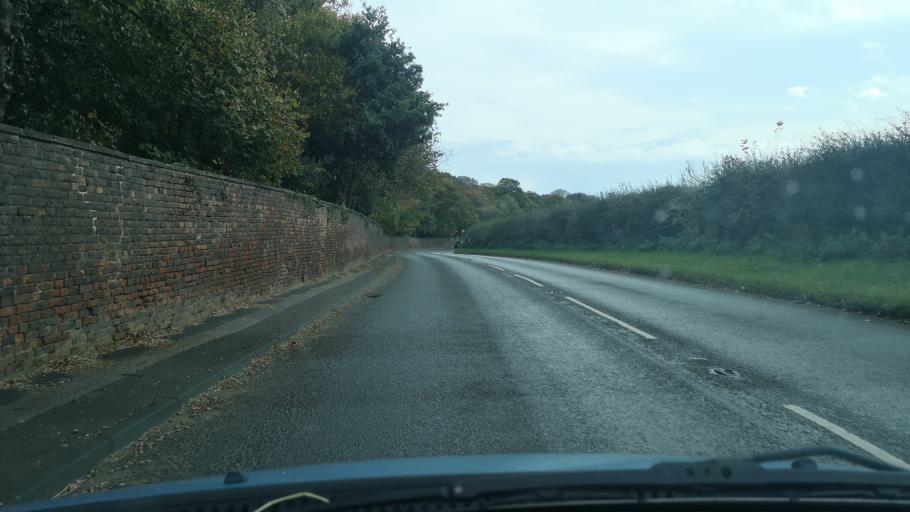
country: GB
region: England
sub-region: City and Borough of Wakefield
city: Sharlston
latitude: 53.6539
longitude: -1.3964
